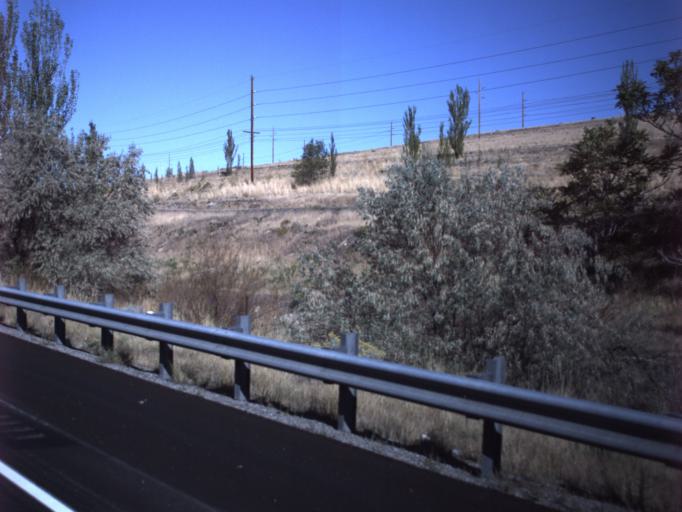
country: US
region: Utah
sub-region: Salt Lake County
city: Magna
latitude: 40.7168
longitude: -112.1330
